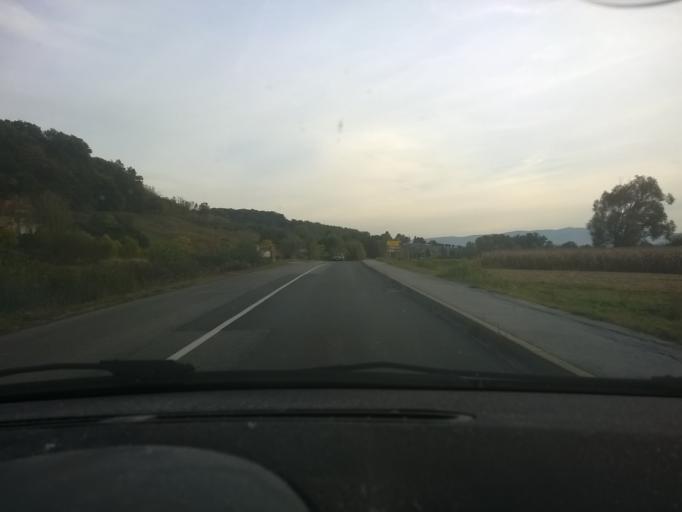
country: HR
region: Krapinsko-Zagorska
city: Zabok
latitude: 46.0867
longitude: 15.9149
